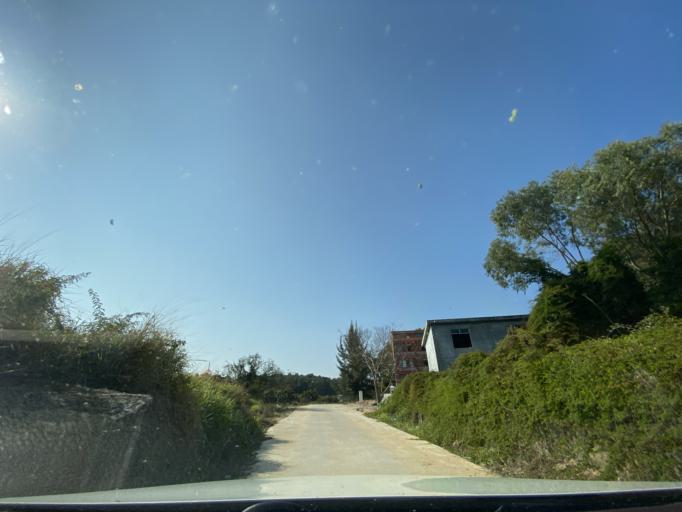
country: CN
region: Hainan
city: Haitangwan
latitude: 18.3972
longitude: 109.7695
